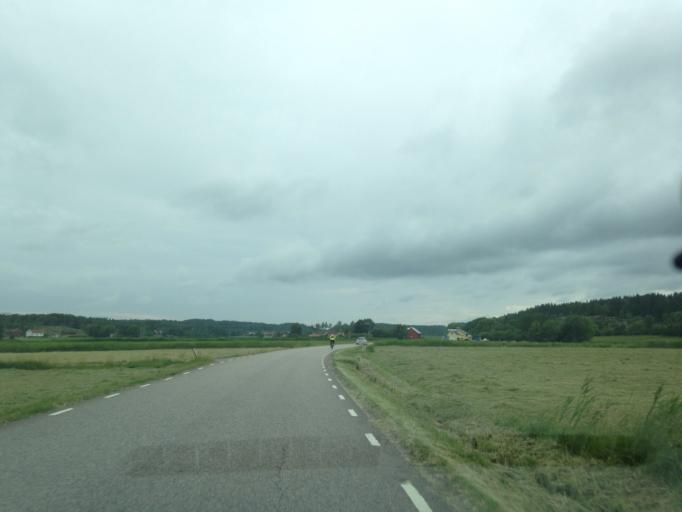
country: SE
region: Vaestra Goetaland
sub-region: Kungalvs Kommun
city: Kode
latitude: 57.8299
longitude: 11.8093
